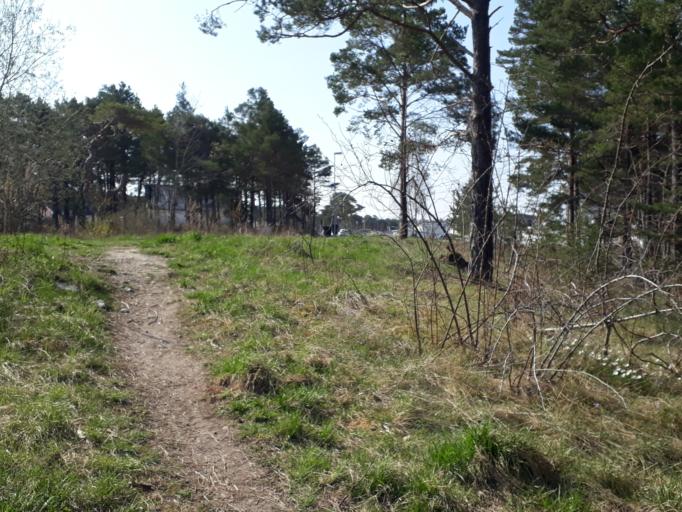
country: SE
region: Gotland
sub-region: Gotland
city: Visby
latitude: 57.6714
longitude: 18.3354
